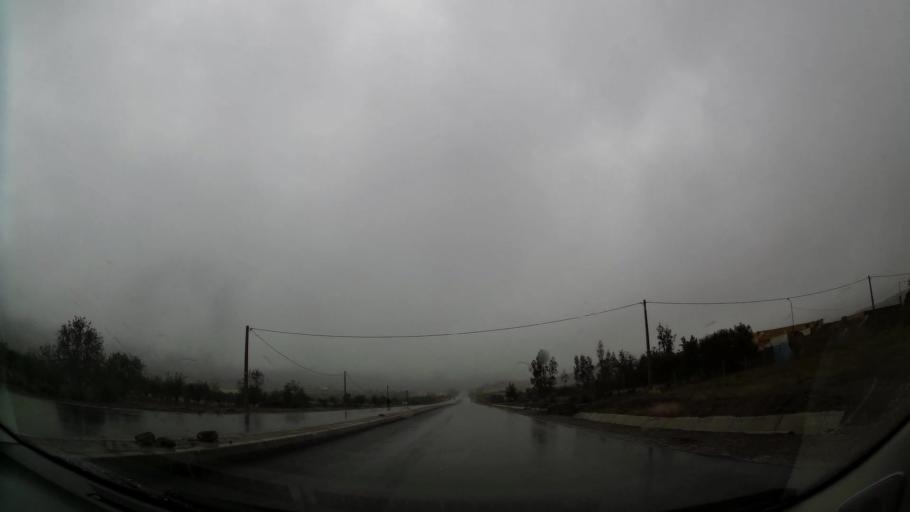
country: MA
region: Oriental
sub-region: Nador
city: Midar
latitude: 34.8446
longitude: -3.7213
